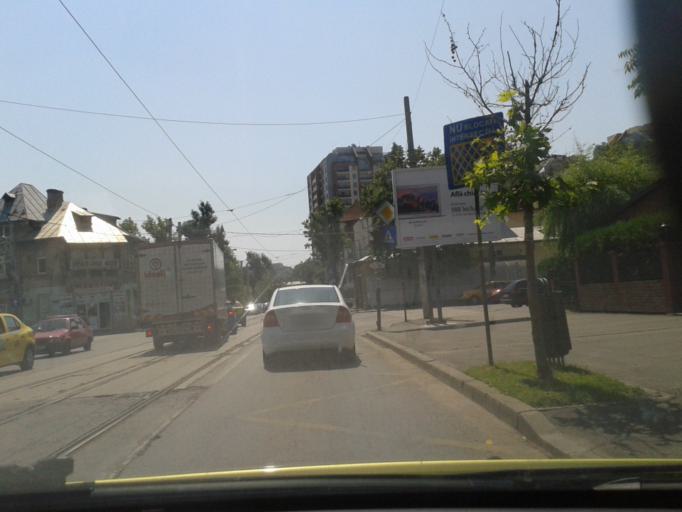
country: RO
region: Bucuresti
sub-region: Municipiul Bucuresti
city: Bucharest
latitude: 44.4221
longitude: 26.1307
